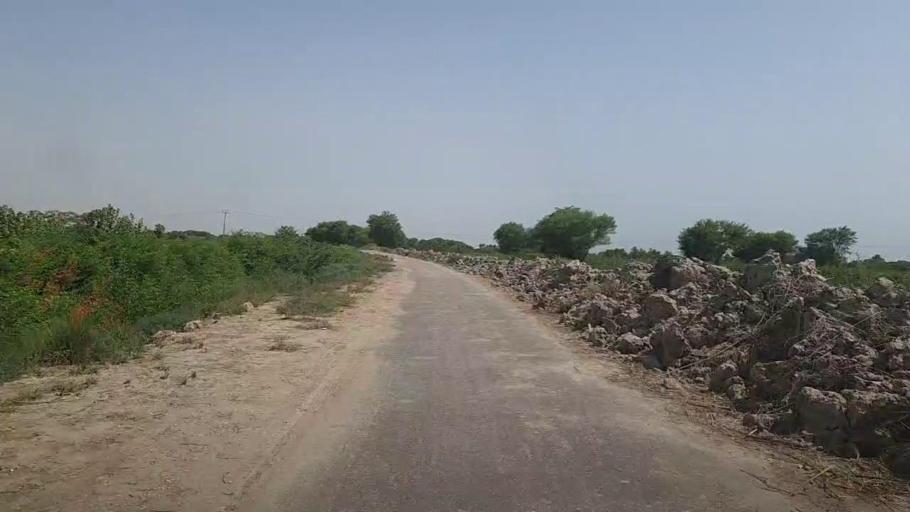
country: PK
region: Sindh
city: Pad Idan
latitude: 26.8134
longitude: 68.3279
